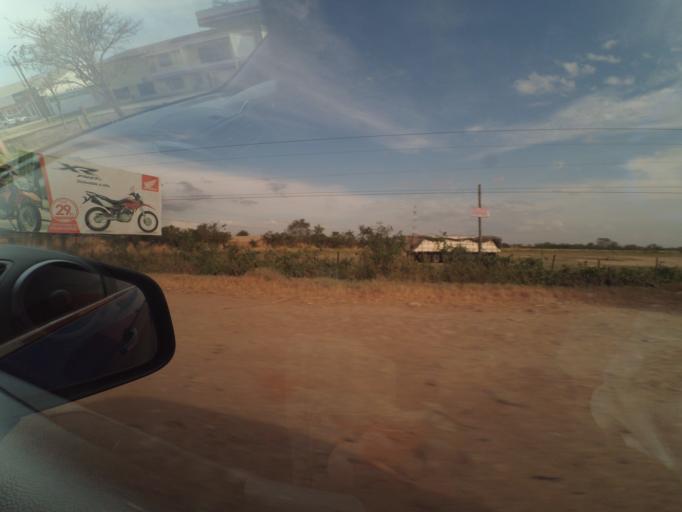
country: BO
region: Santa Cruz
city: Okinawa Numero Uno
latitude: -17.2223
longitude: -62.9039
